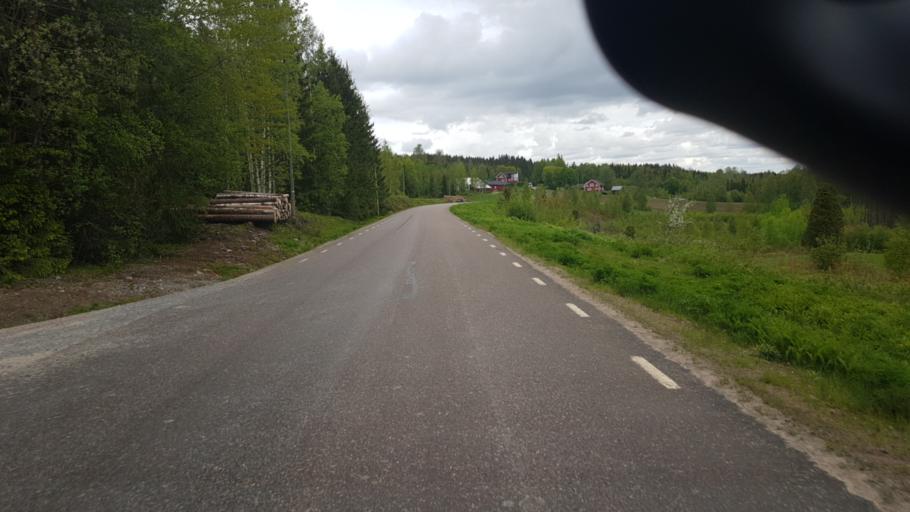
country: SE
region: Vaermland
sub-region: Arvika Kommun
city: Arvika
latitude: 59.7810
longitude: 12.7726
